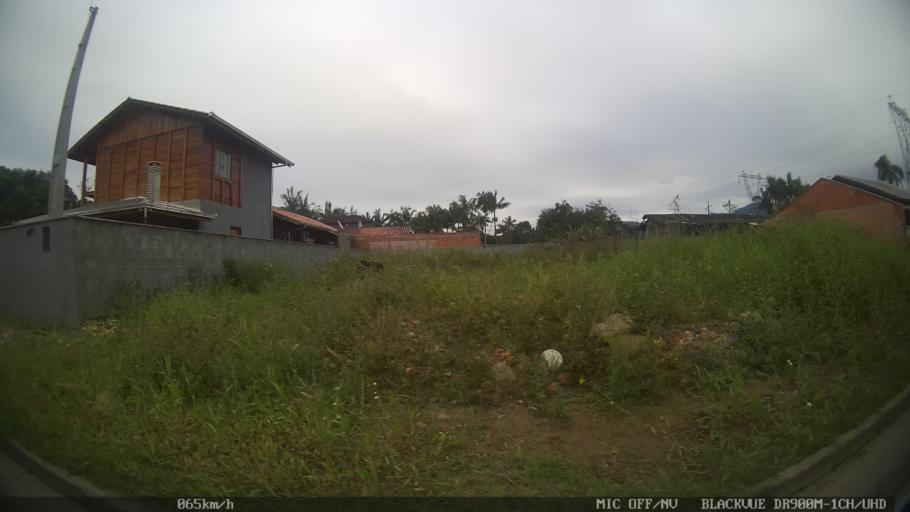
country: BR
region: Santa Catarina
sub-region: Joinville
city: Joinville
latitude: -26.3182
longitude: -48.9142
